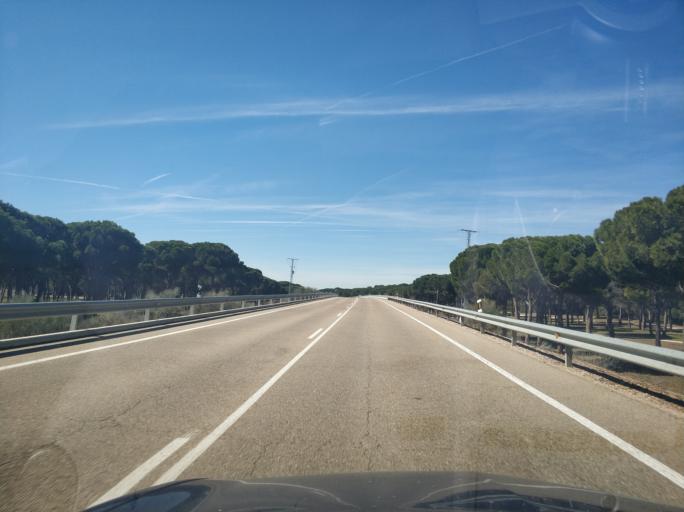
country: ES
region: Castille and Leon
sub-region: Provincia de Valladolid
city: Viana de Cega
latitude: 41.5331
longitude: -4.7342
